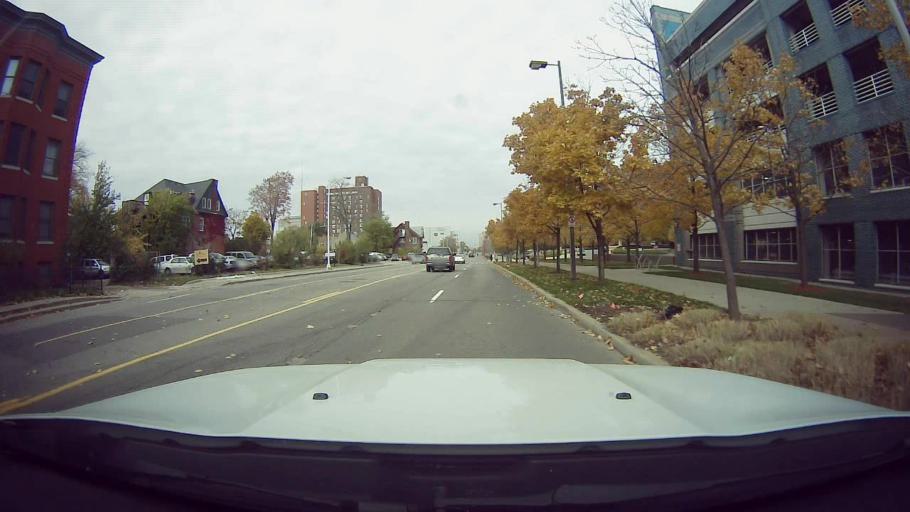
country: US
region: Michigan
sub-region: Wayne County
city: Detroit
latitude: 42.3541
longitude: -83.0595
